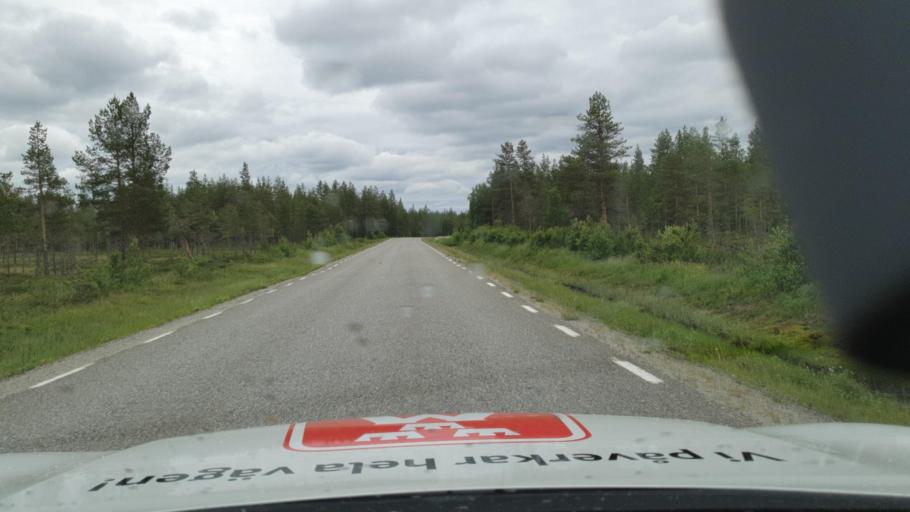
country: SE
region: Vaesterbotten
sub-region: Lycksele Kommun
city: Lycksele
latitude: 64.2589
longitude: 18.2103
